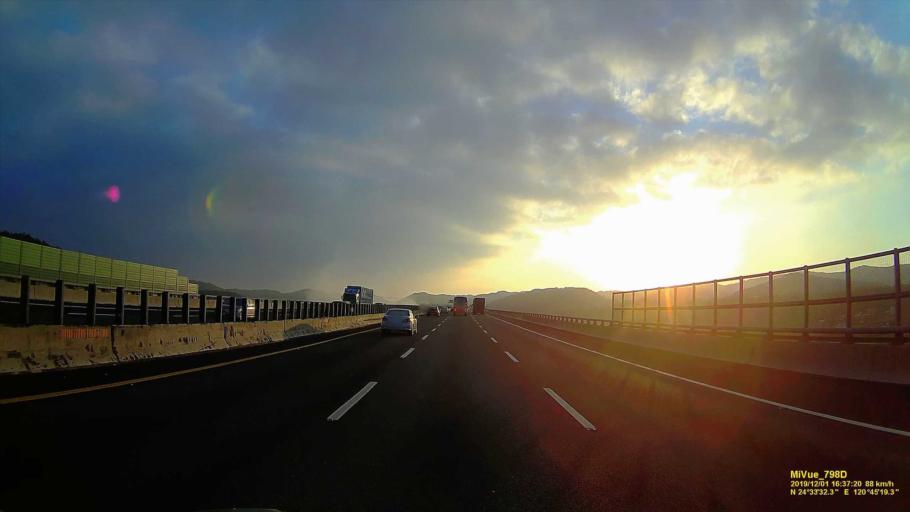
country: TW
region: Taiwan
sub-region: Miaoli
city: Miaoli
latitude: 24.5609
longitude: 120.7562
